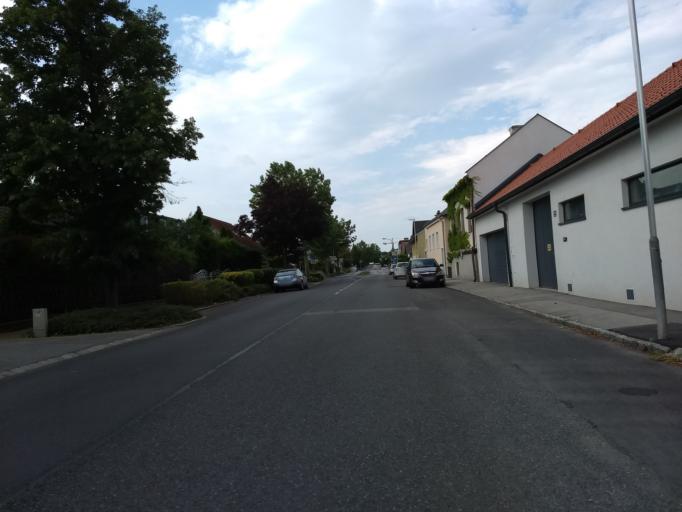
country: AT
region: Lower Austria
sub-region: Politischer Bezirk Modling
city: Guntramsdorf
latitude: 48.0519
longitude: 16.3205
